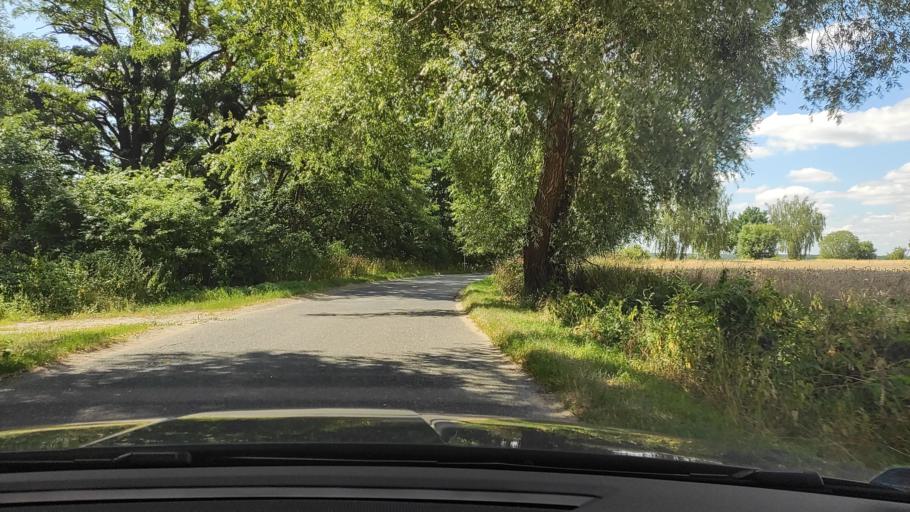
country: PL
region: Greater Poland Voivodeship
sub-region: Powiat poznanski
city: Kobylnica
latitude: 52.4854
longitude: 17.1372
